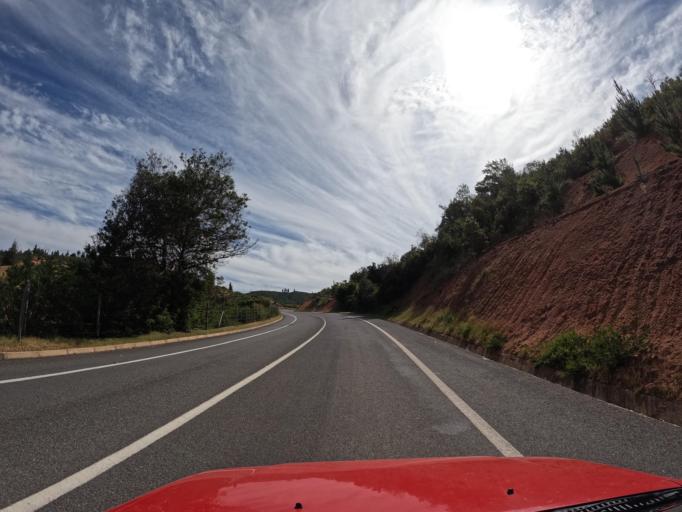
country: CL
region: Maule
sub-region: Provincia de Talca
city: Talca
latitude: -35.1574
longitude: -71.9635
